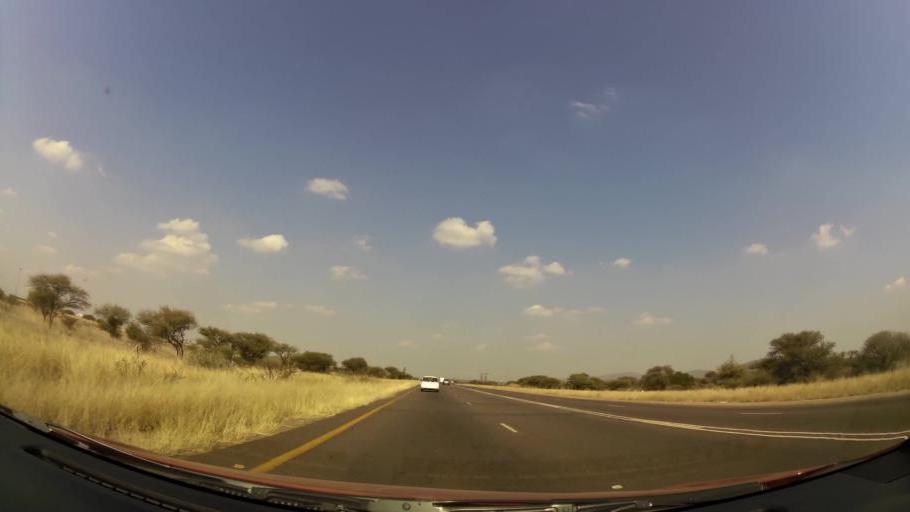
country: ZA
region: North-West
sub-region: Bojanala Platinum District Municipality
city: Mogwase
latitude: -25.4112
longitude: 27.0763
